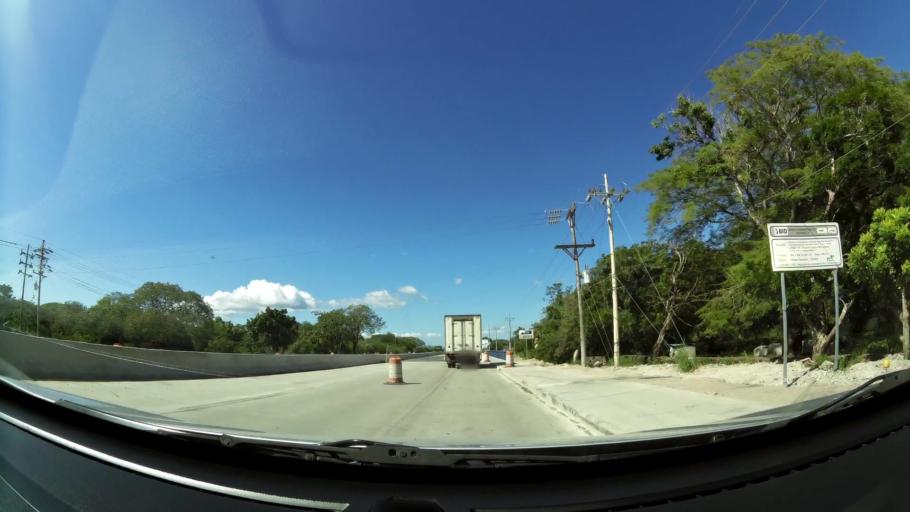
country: CR
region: Guanacaste
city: Liberia
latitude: 10.6209
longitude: -85.4398
